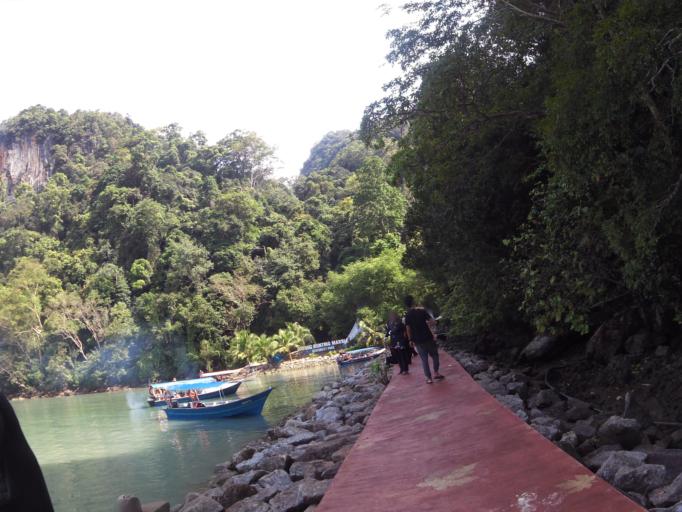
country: MY
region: Kedah
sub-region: Langkawi
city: Kuah
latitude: 6.2081
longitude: 99.7821
